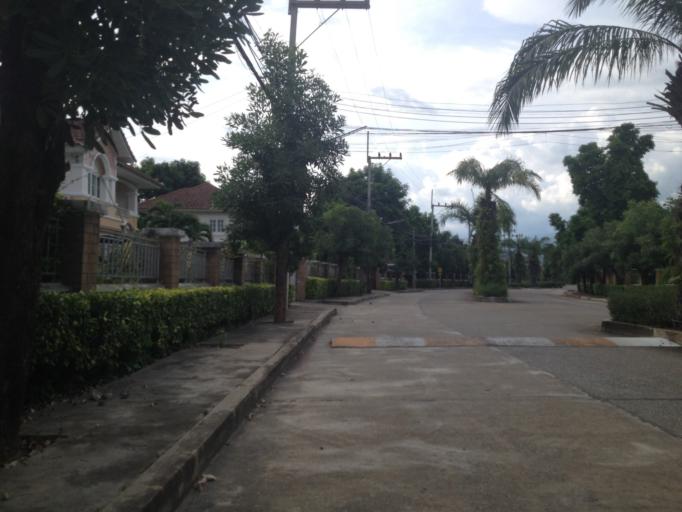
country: TH
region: Chiang Mai
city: Hang Dong
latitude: 18.7138
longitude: 98.9235
